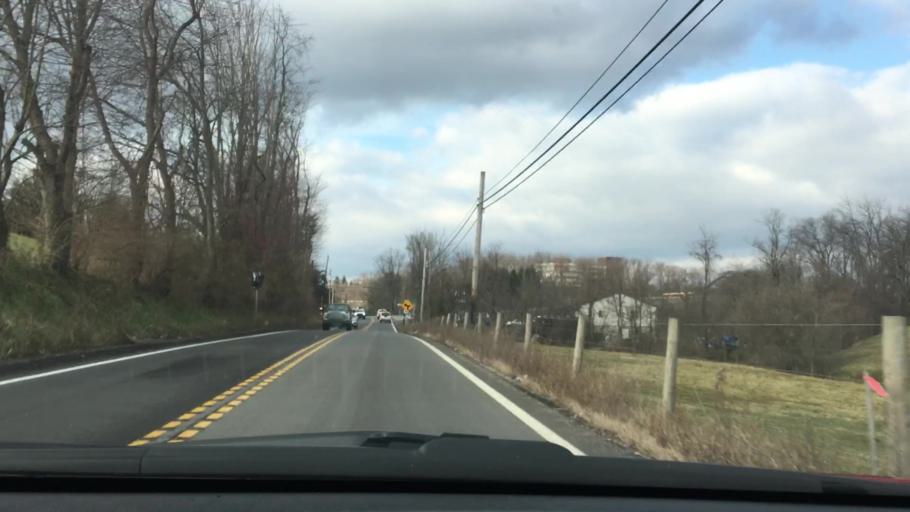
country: US
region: Pennsylvania
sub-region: Allegheny County
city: Enlow
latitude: 40.4339
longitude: -80.2070
